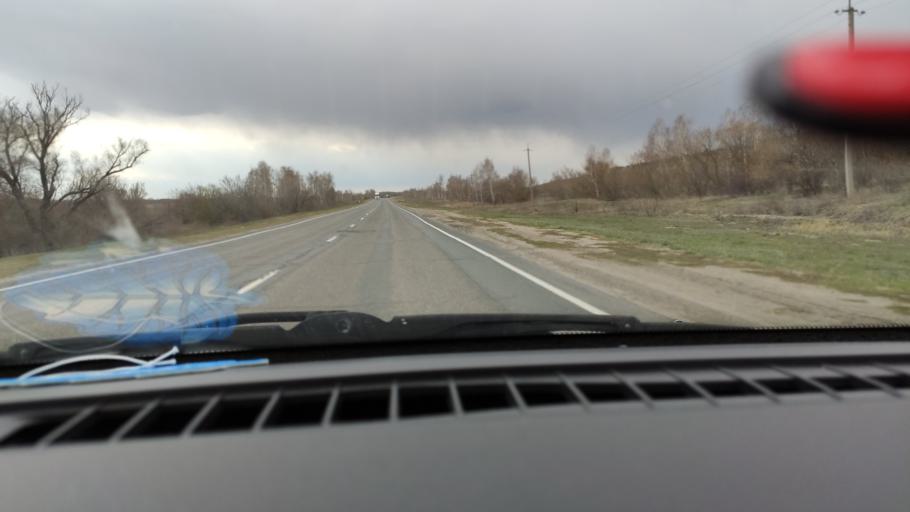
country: RU
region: Saratov
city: Sinodskoye
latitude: 52.0600
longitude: 46.7628
